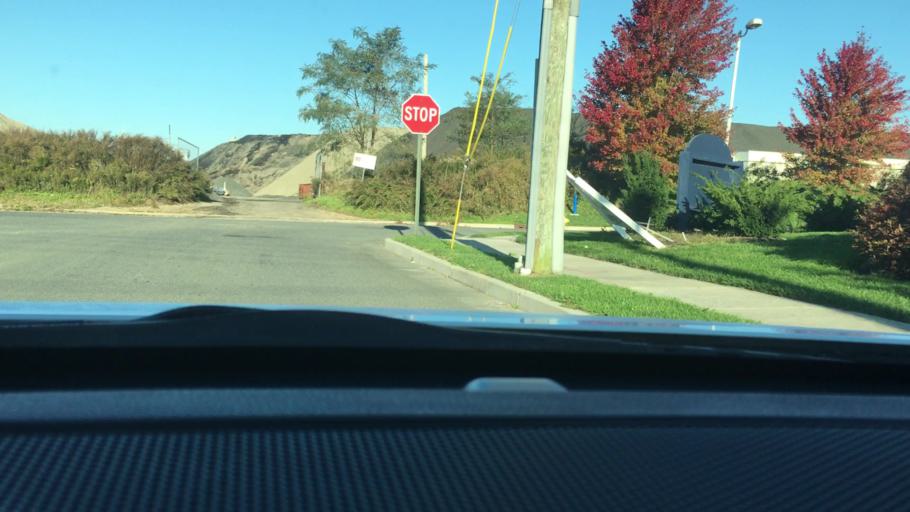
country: US
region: New Jersey
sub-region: Atlantic County
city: Pleasantville
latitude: 39.4013
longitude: -74.5347
